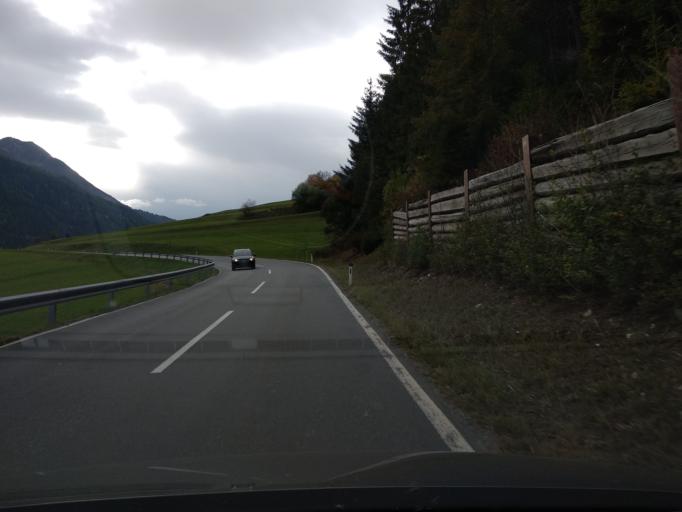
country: AT
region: Tyrol
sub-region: Politischer Bezirk Landeck
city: Flirsch
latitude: 47.1521
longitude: 10.3560
